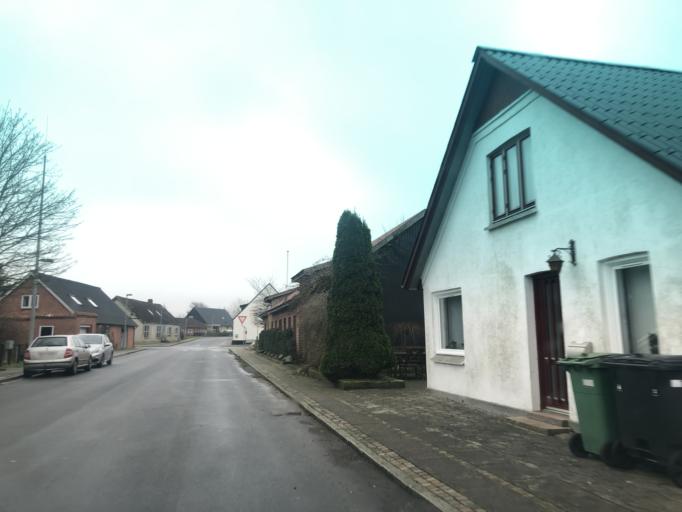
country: DK
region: Central Jutland
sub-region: Struer Kommune
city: Struer
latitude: 56.4352
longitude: 8.5829
